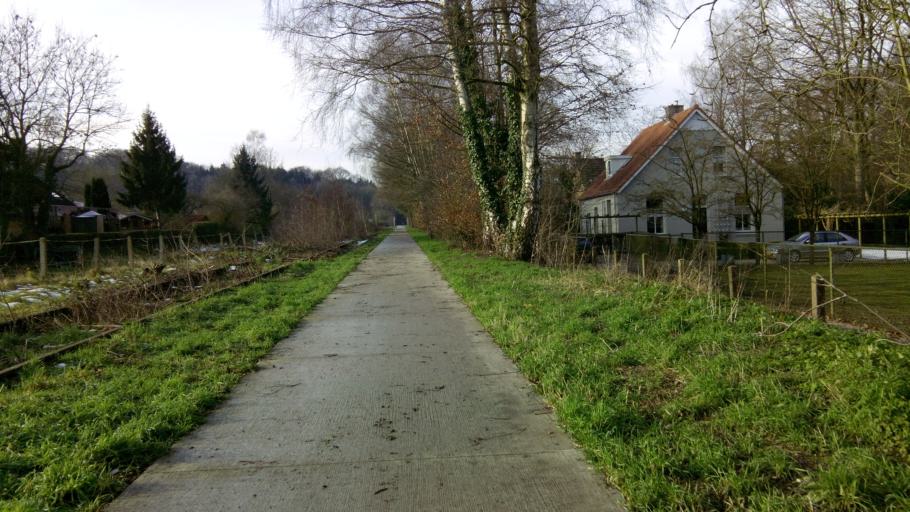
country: NL
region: Gelderland
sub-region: Gemeente Groesbeek
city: Groesbeek
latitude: 51.7780
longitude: 5.9309
